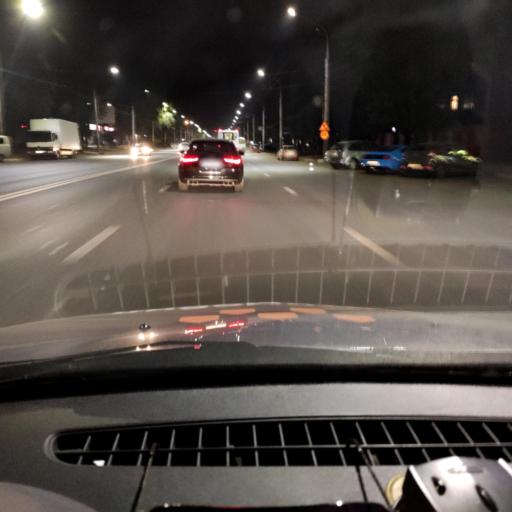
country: RU
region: Voronezj
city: Voronezh
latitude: 51.6421
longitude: 39.2369
